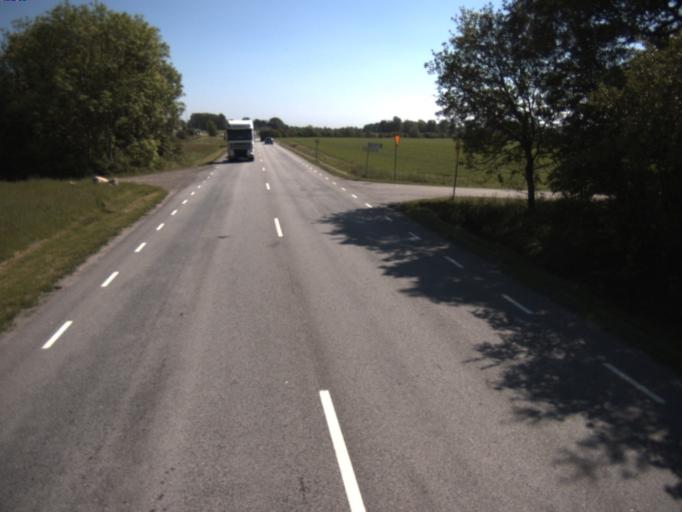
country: SE
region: Skane
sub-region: Helsingborg
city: Odakra
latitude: 56.0503
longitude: 12.7739
